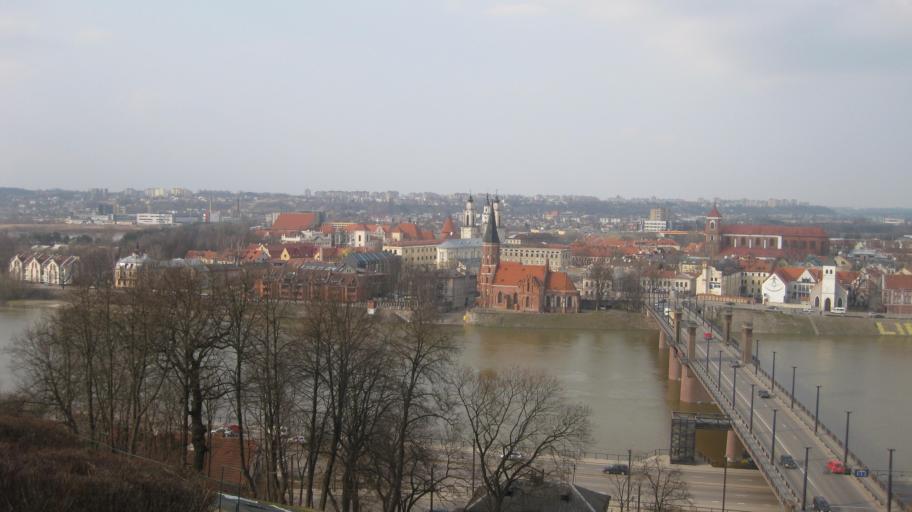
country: LT
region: Kauno apskritis
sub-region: Kaunas
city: Aleksotas
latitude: 54.8914
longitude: 23.8866
